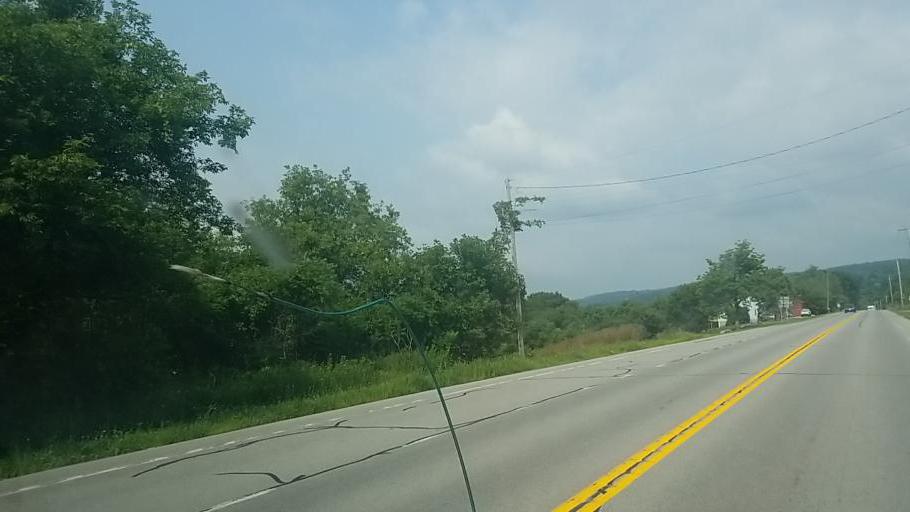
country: US
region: New York
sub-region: Montgomery County
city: Saint Johnsville
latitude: 42.9903
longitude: -74.6540
